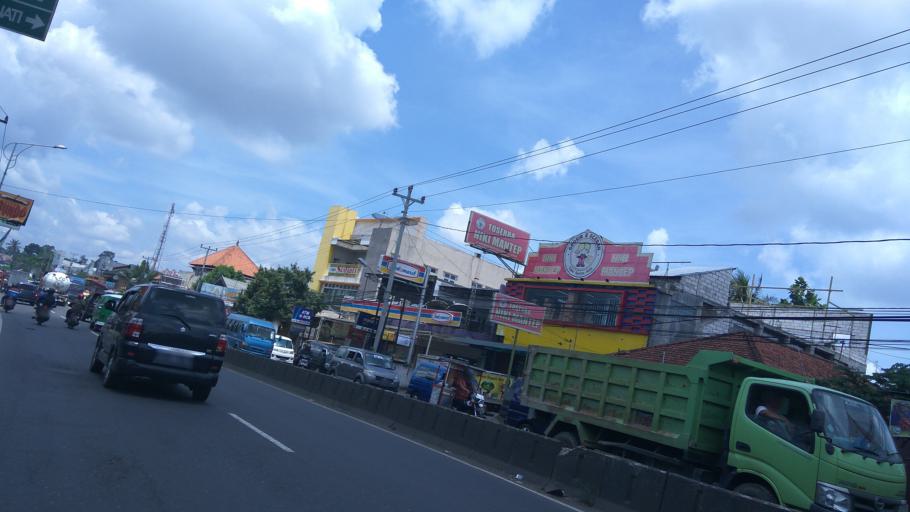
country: ID
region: Central Java
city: Ungaran
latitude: -7.1853
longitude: 110.4271
